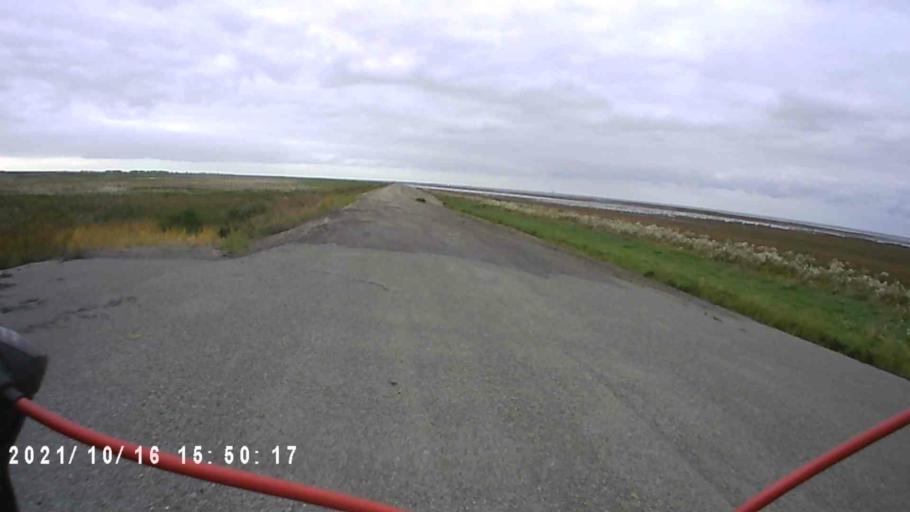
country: NL
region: Friesland
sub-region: Gemeente Dongeradeel
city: Anjum
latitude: 53.4033
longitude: 6.1382
